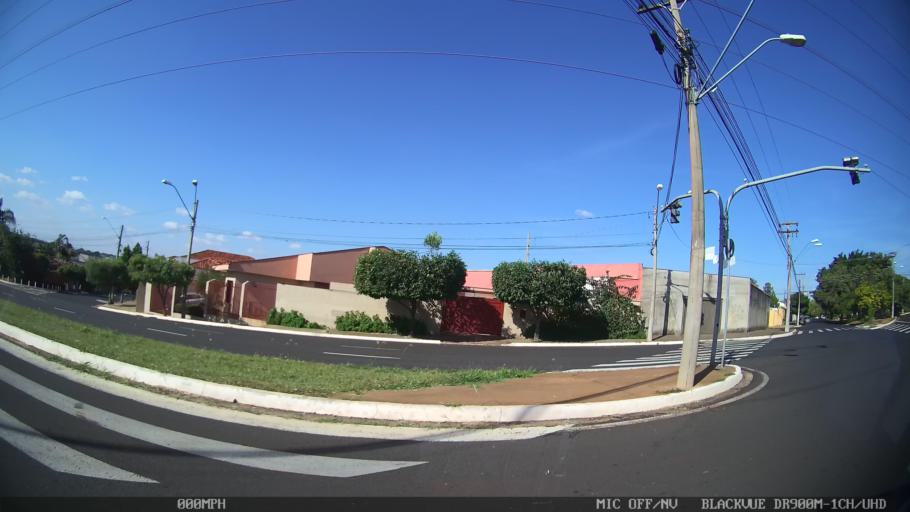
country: BR
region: Sao Paulo
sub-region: Ribeirao Preto
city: Ribeirao Preto
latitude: -21.1842
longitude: -47.7832
